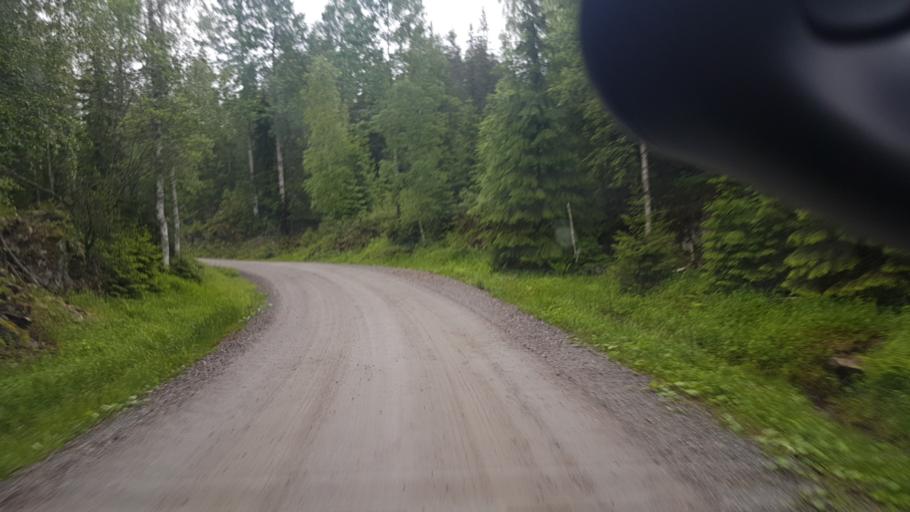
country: NO
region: Ostfold
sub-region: Romskog
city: Romskog
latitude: 59.7138
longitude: 11.9851
